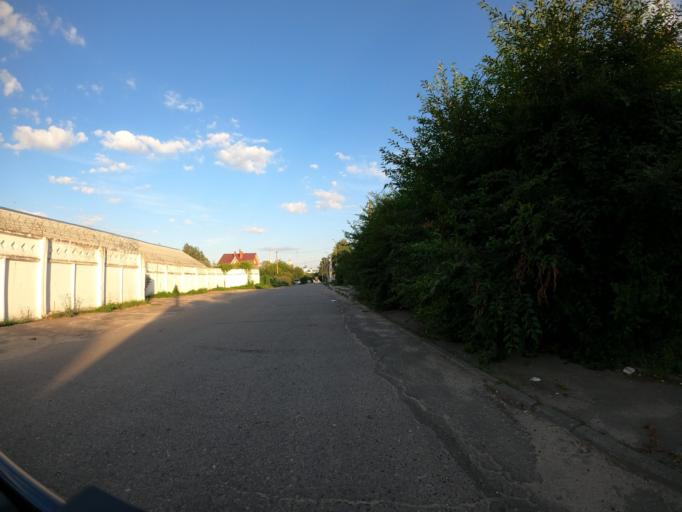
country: RU
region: Moskovskaya
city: Raduzhnyy
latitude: 55.1093
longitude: 38.7488
